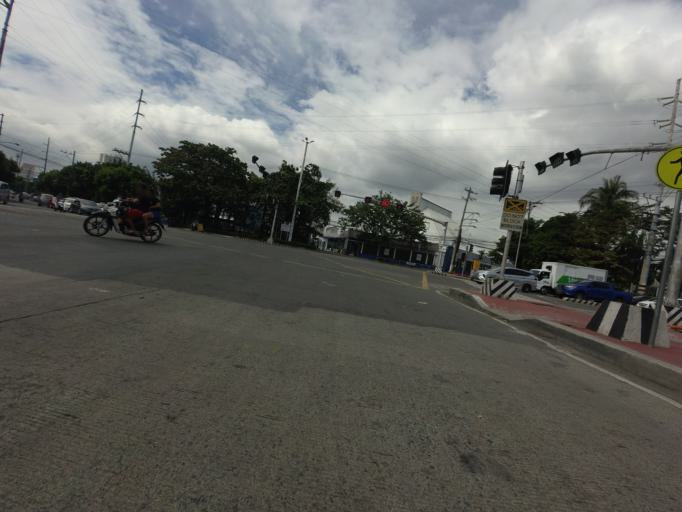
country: PH
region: Metro Manila
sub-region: City of Manila
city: Quiapo
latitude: 14.5854
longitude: 120.9940
